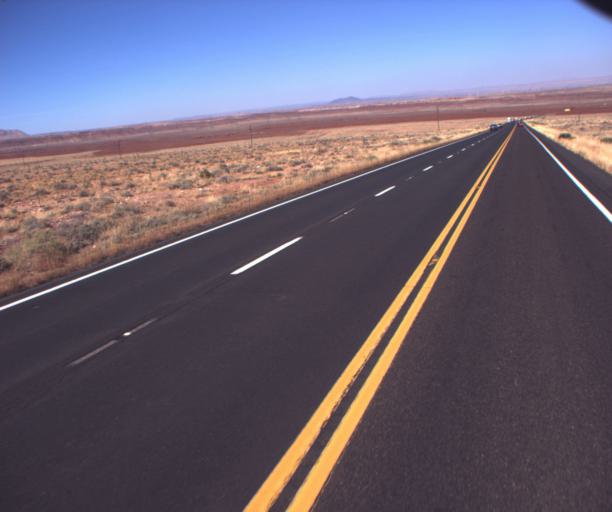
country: US
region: Arizona
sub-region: Coconino County
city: Tuba City
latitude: 35.7635
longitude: -111.4659
